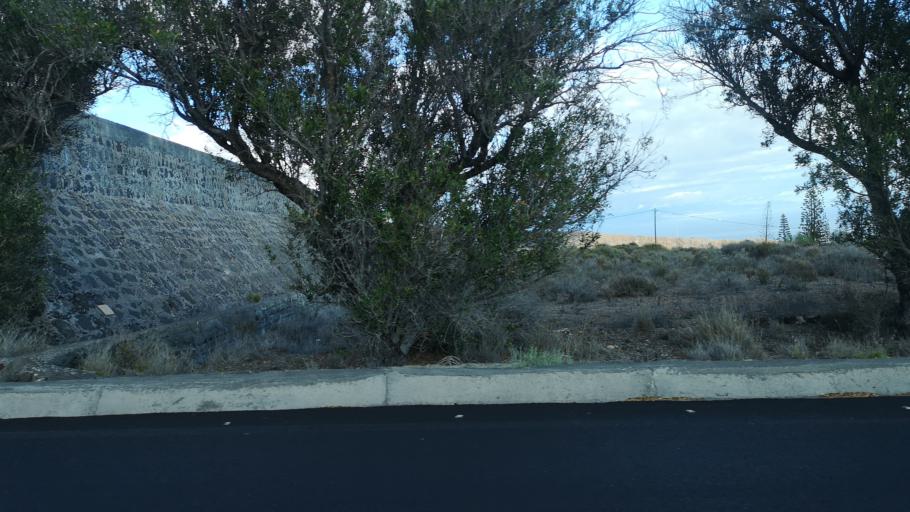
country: ES
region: Canary Islands
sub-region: Provincia de Santa Cruz de Tenerife
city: Alajero
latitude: 28.0494
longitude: -17.1987
